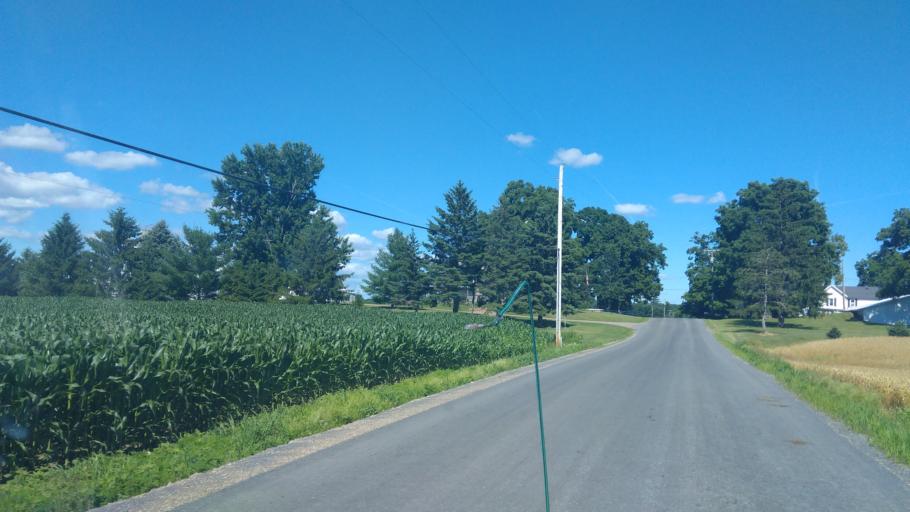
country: US
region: New York
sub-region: Wayne County
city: Clyde
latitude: 43.0261
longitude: -76.8957
